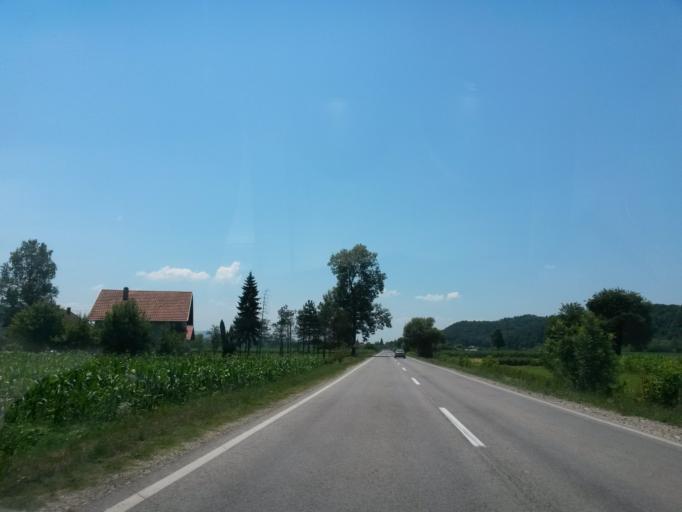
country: BA
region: Federation of Bosnia and Herzegovina
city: Lukavica
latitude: 44.8954
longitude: 18.0957
